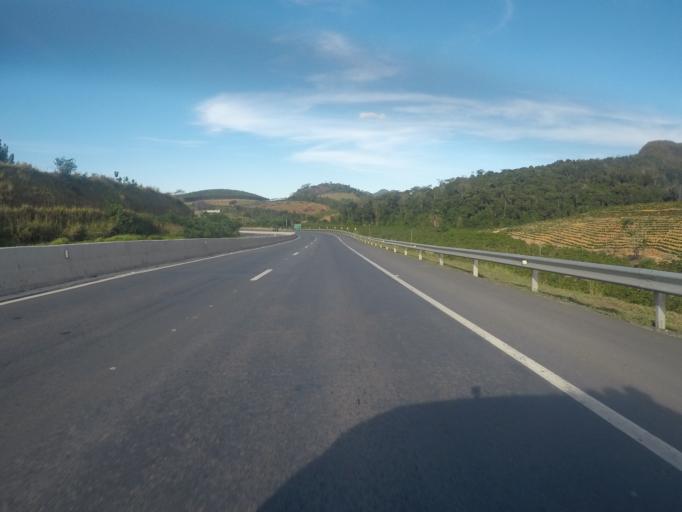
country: BR
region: Espirito Santo
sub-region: Ibiracu
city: Ibiracu
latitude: -19.8657
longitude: -40.3868
